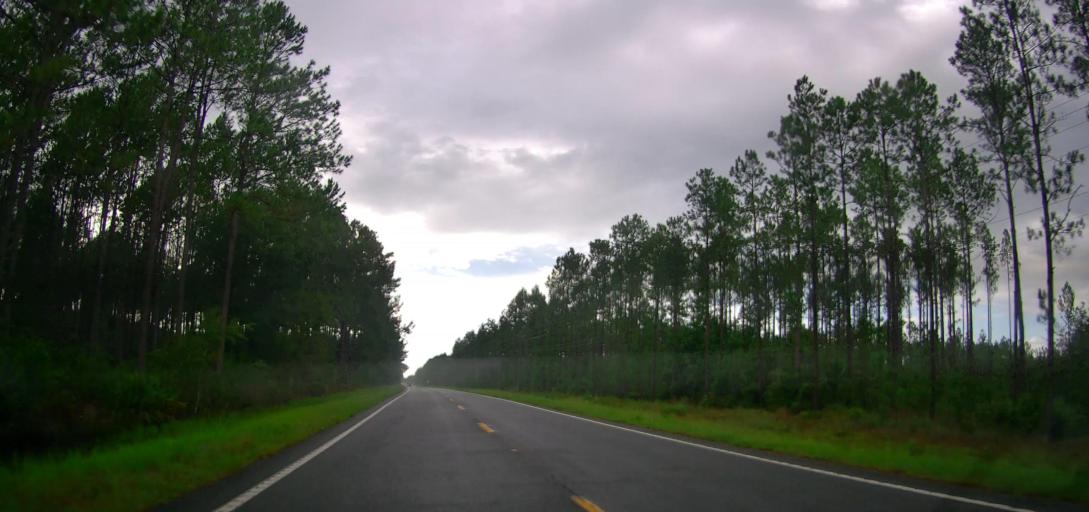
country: US
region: Georgia
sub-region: Ware County
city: Deenwood
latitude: 31.2722
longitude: -82.5271
